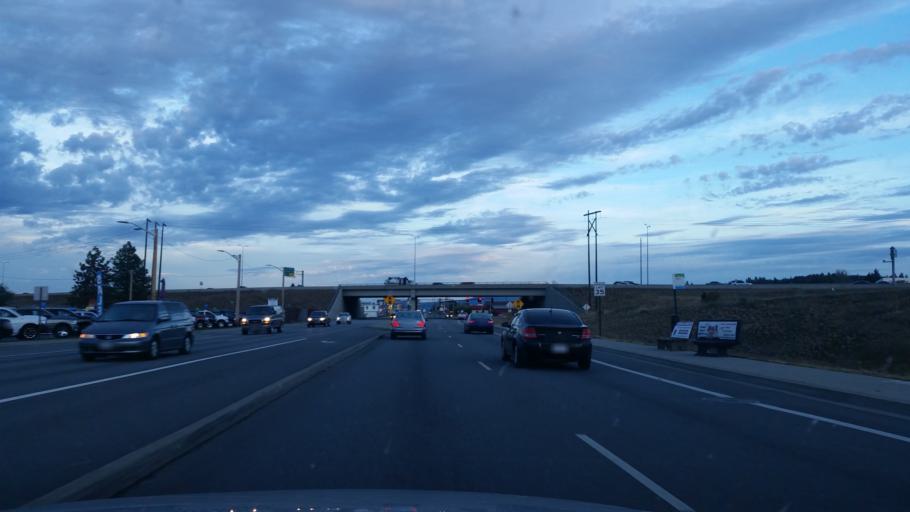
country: US
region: Washington
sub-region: Spokane County
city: Millwood
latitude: 47.6570
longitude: -117.3250
